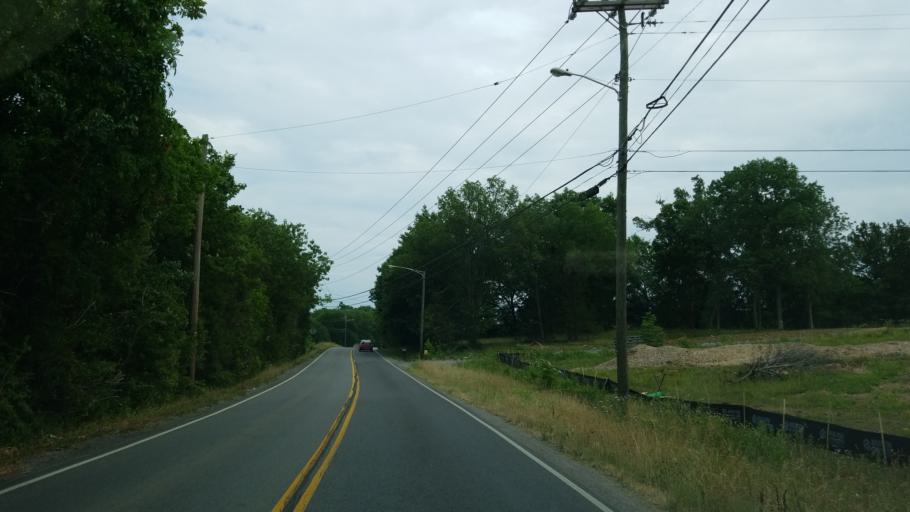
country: US
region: Tennessee
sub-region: Rutherford County
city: La Vergne
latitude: 36.0609
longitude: -86.6043
